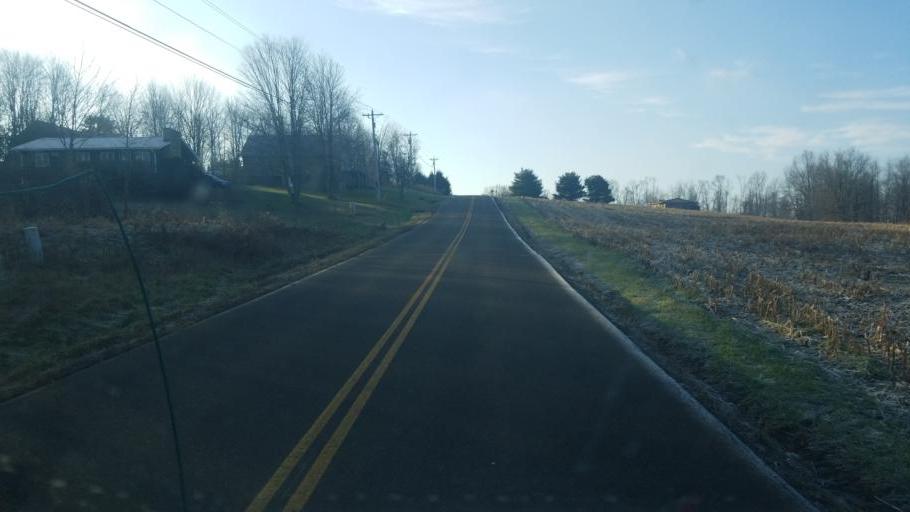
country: US
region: Ohio
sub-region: Knox County
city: Gambier
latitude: 40.4479
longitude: -82.3663
